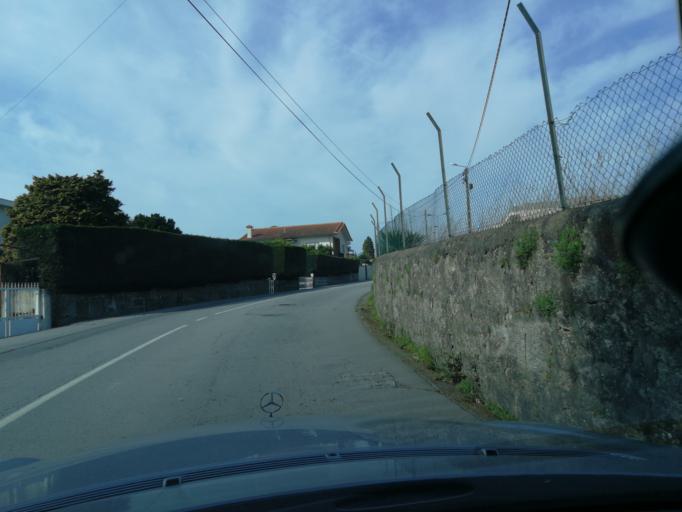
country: PT
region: Braga
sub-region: Vila Nova de Famalicao
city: Vila Nova de Famalicao
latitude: 41.4246
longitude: -8.5189
